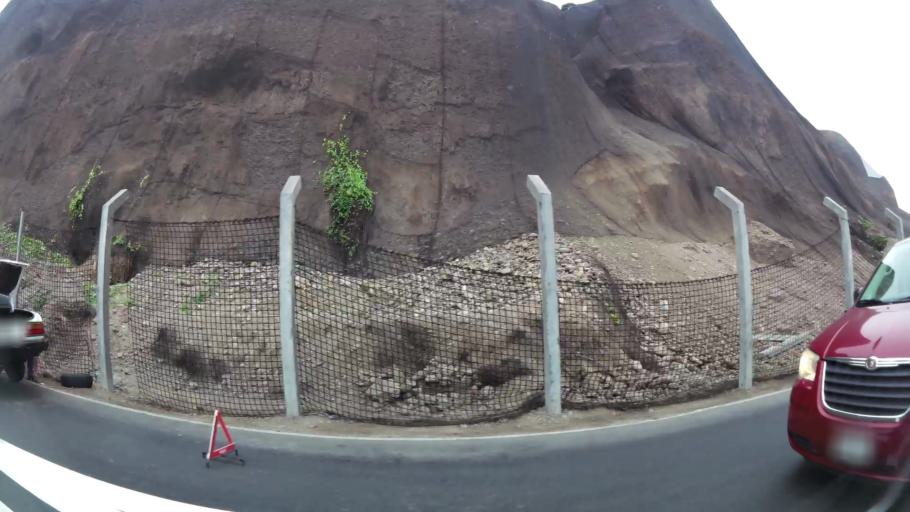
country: PE
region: Lima
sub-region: Lima
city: San Isidro
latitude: -12.1158
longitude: -77.0500
